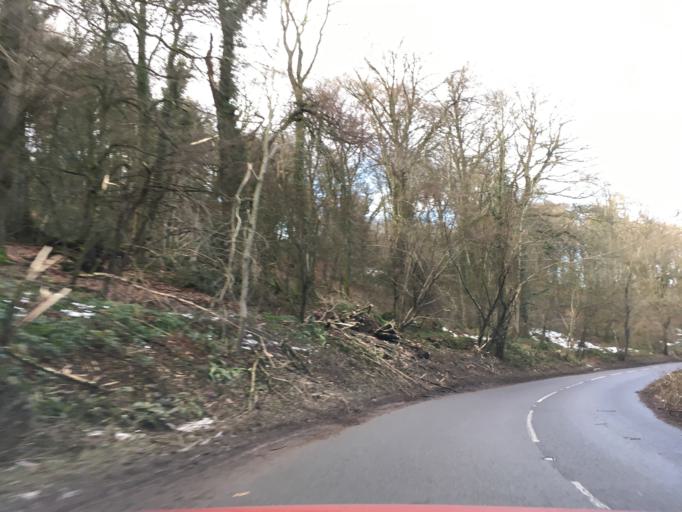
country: GB
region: Wales
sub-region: Monmouthshire
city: Monmouth
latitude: 51.8143
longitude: -2.6805
